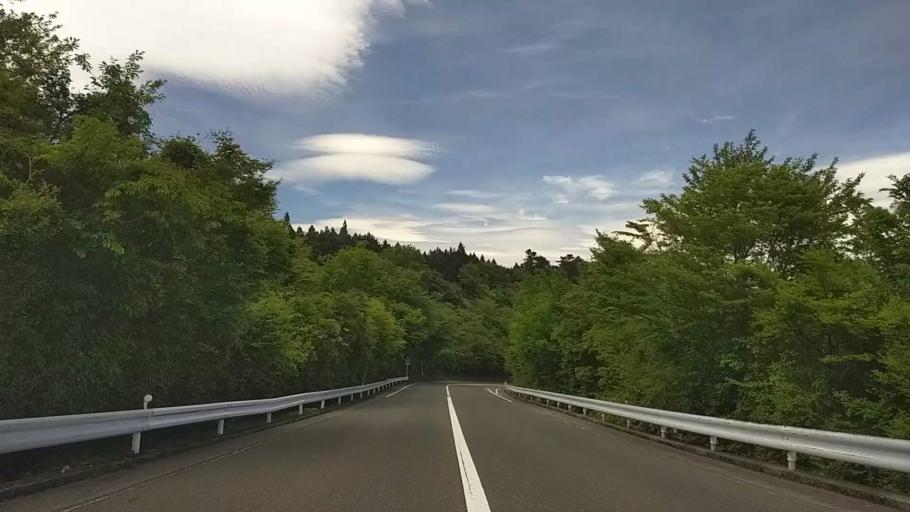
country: JP
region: Kanagawa
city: Yugawara
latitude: 35.2039
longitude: 139.0887
